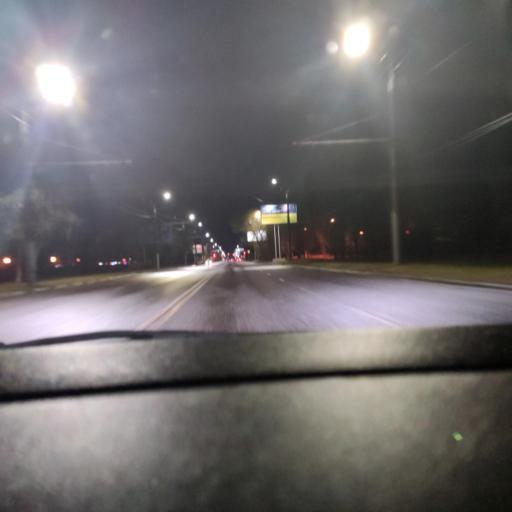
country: RU
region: Voronezj
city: Pridonskoy
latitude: 51.6533
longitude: 39.1250
